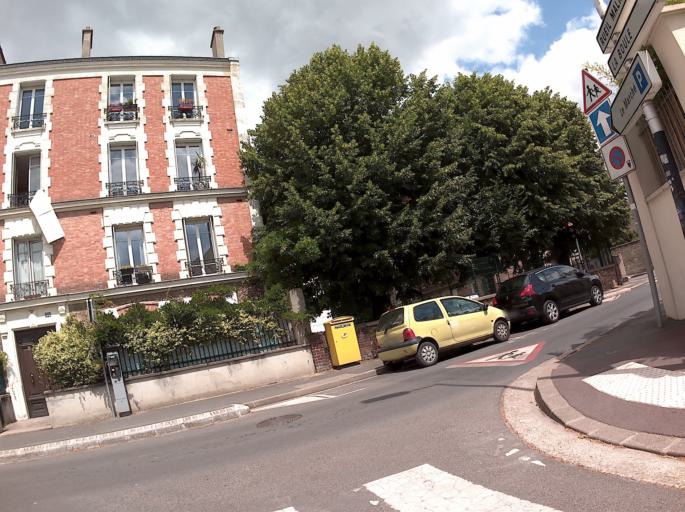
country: FR
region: Ile-de-France
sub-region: Departement des Hauts-de-Seine
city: Rueil-Malmaison
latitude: 48.8901
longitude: 2.1905
